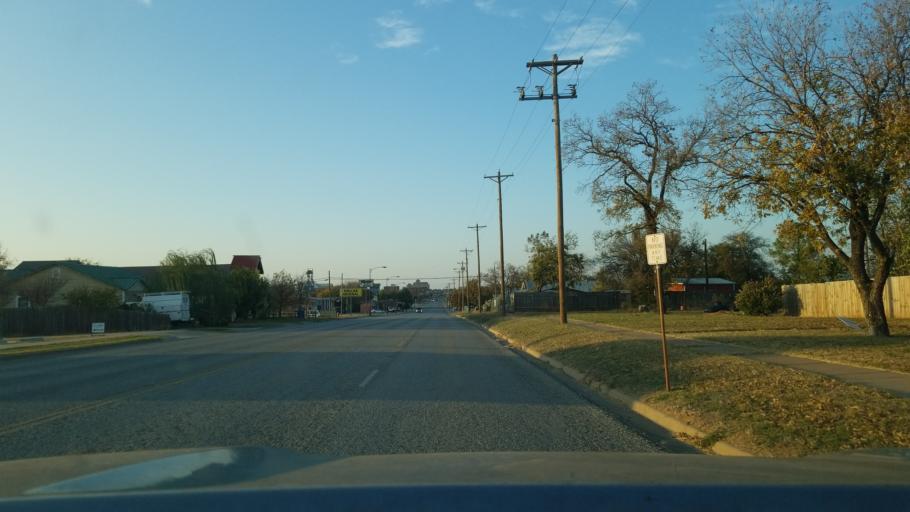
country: US
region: Texas
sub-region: Eastland County
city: Cisco
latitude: 32.3814
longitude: -98.9749
